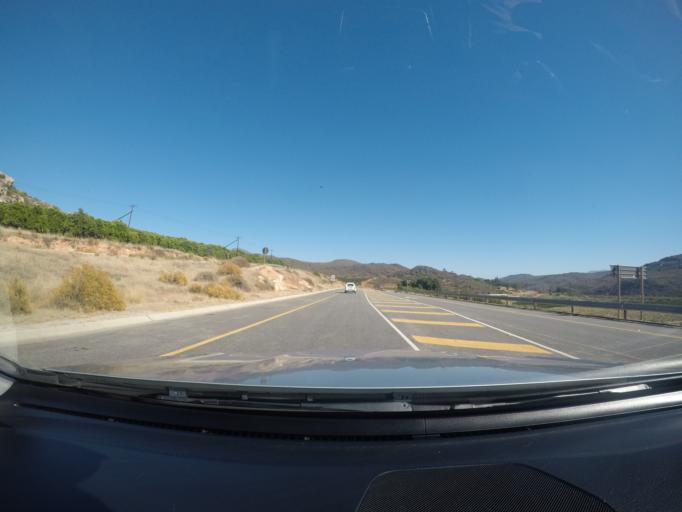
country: ZA
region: Western Cape
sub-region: West Coast District Municipality
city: Clanwilliam
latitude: -32.4359
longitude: 18.9552
